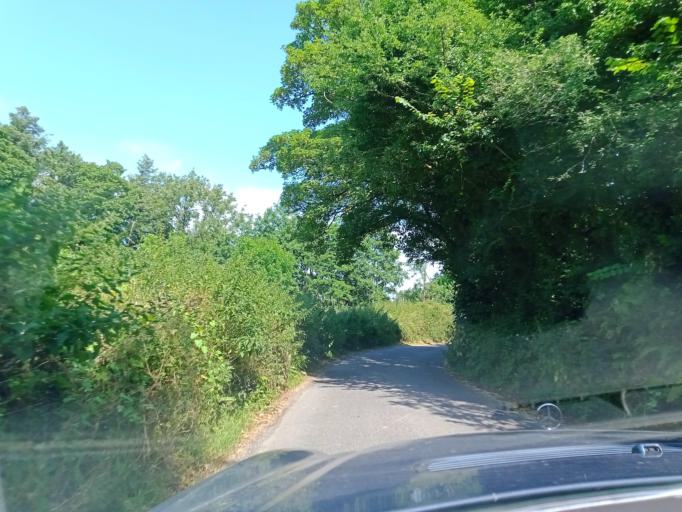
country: IE
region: Leinster
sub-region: Kilkenny
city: Mooncoin
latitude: 52.2768
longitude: -7.2384
